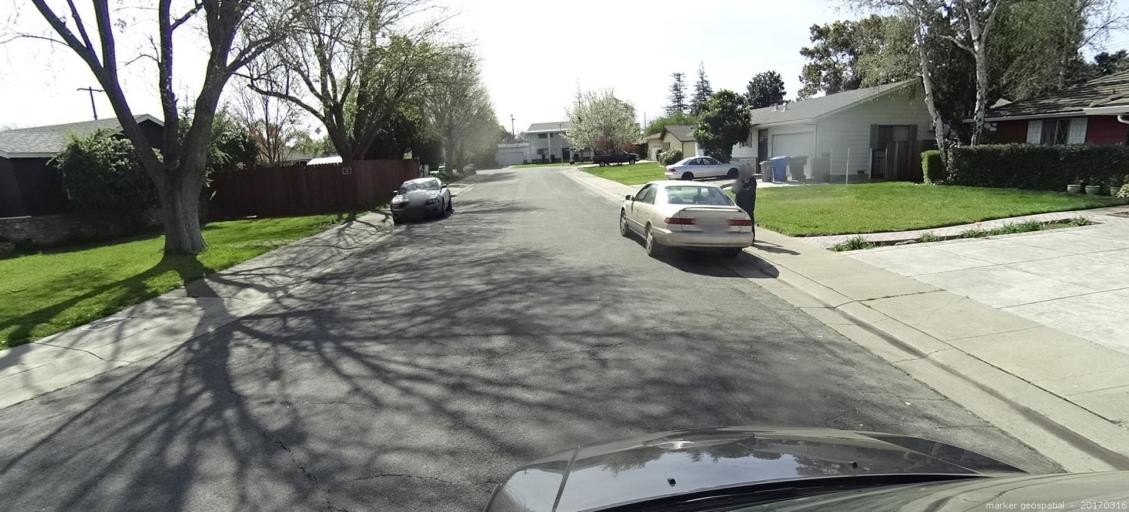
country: US
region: California
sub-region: Sacramento County
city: Parkway
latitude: 38.4981
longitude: -121.5049
